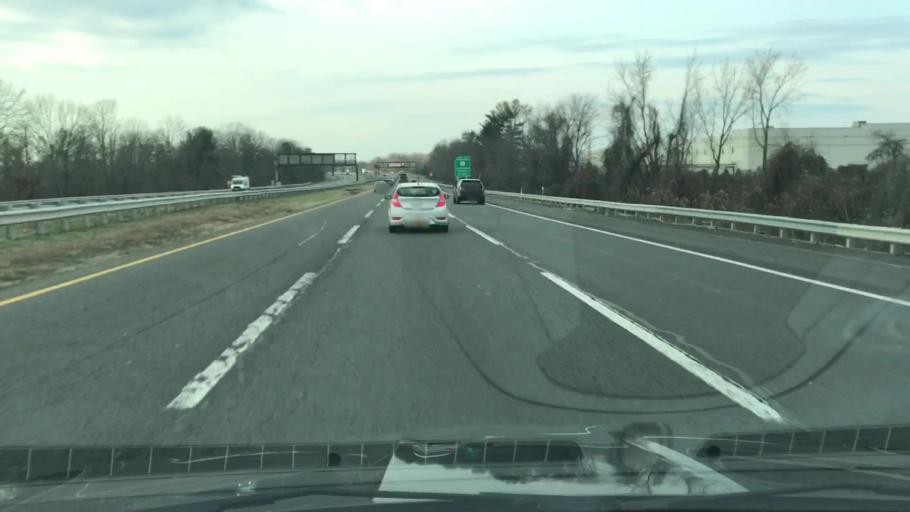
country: US
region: New Jersey
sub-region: Burlington County
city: Roebling
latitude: 40.1068
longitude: -74.7998
